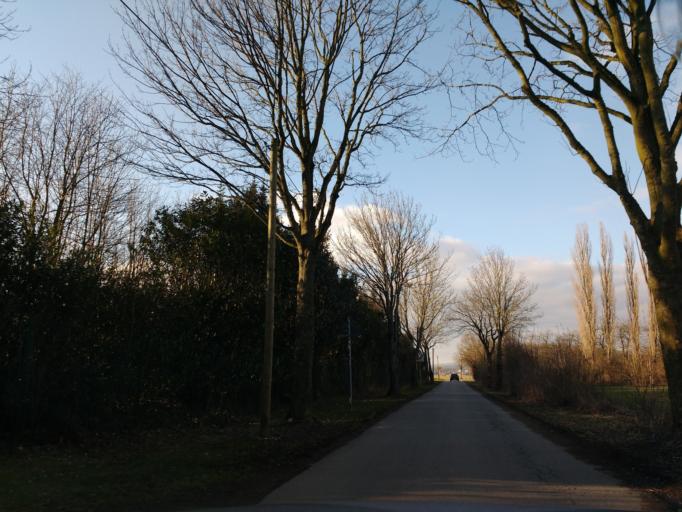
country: DE
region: North Rhine-Westphalia
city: Bad Lippspringe
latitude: 51.7510
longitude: 8.8434
